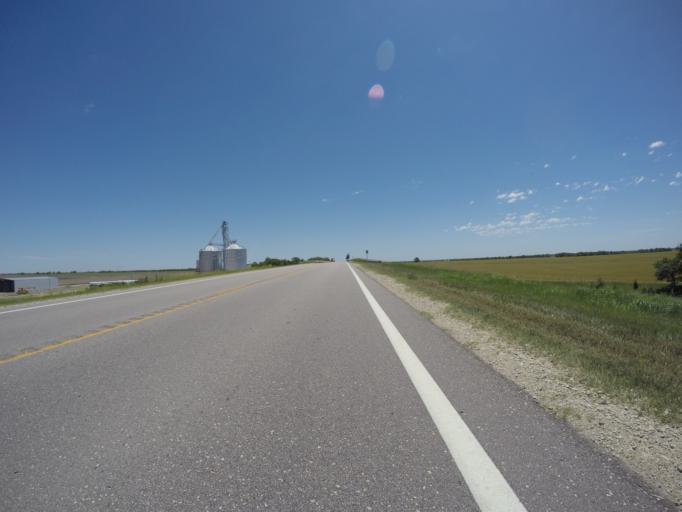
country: US
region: Kansas
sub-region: Republic County
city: Belleville
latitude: 39.8121
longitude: -97.7146
